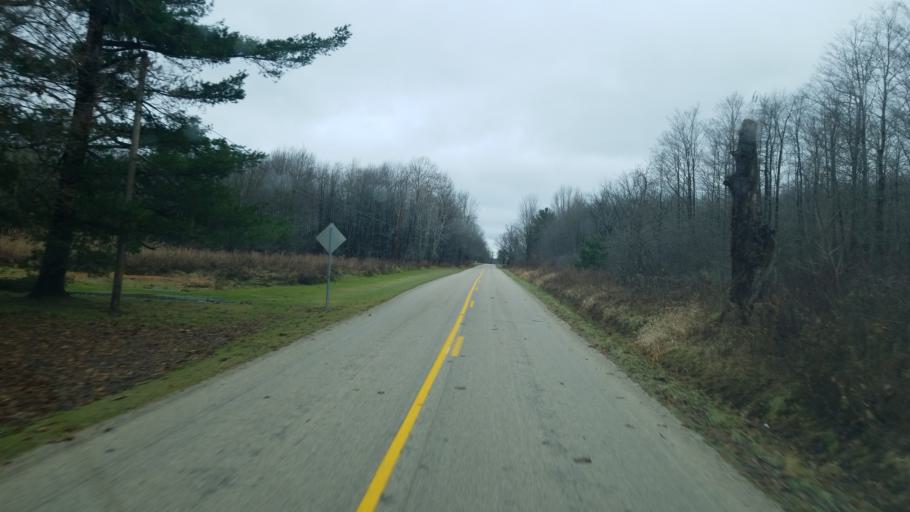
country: US
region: Ohio
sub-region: Ashtabula County
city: Andover
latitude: 41.6937
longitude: -80.6132
